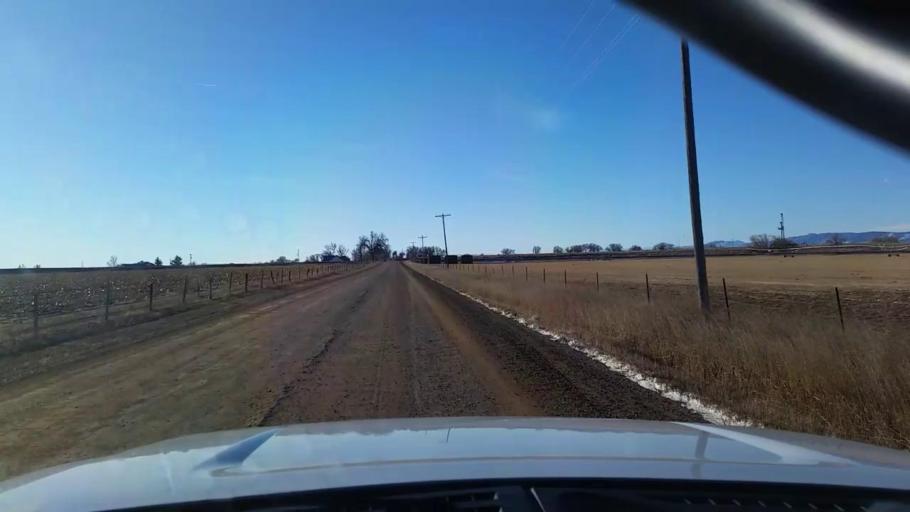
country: US
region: Colorado
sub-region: Larimer County
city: Wellington
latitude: 40.7688
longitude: -105.0382
